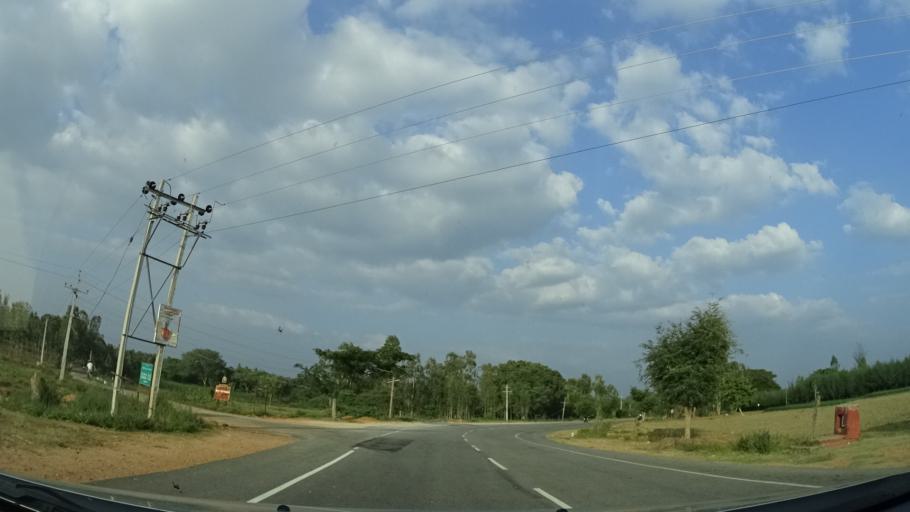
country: IN
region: Karnataka
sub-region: Mandya
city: Malavalli
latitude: 12.3650
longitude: 76.9918
